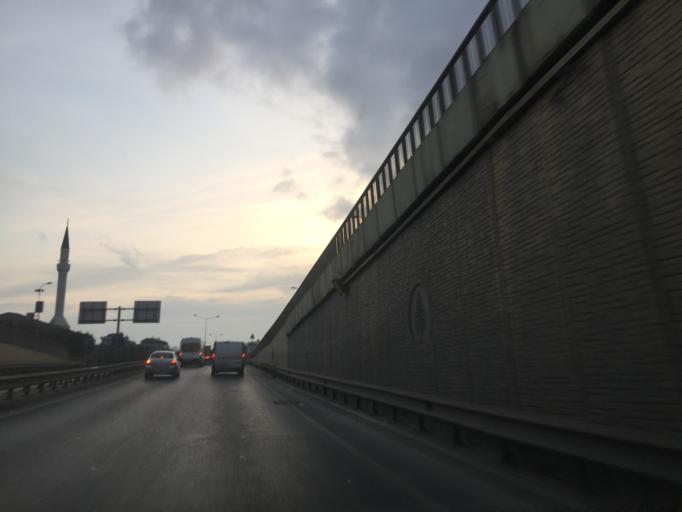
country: TR
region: Istanbul
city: Samandira
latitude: 40.9878
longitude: 29.2251
